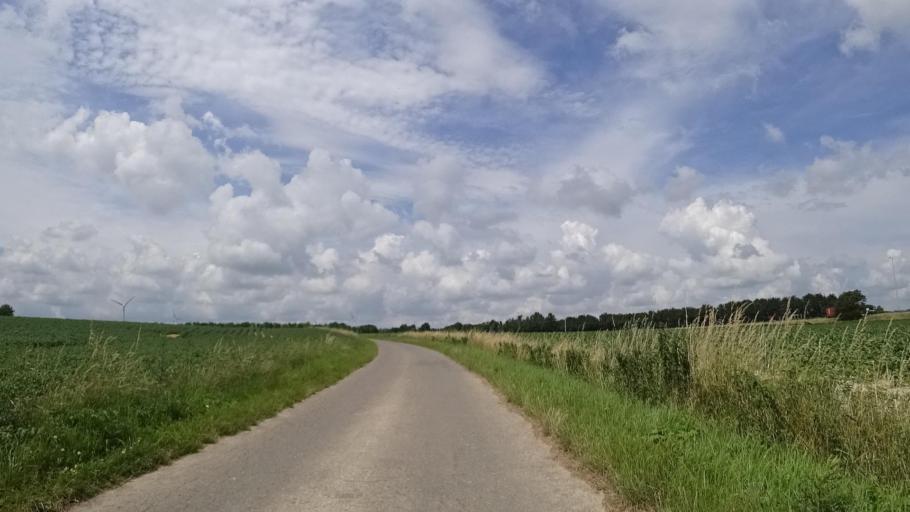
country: BE
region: Wallonia
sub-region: Province du Brabant Wallon
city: Perwez
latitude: 50.5804
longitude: 4.8085
